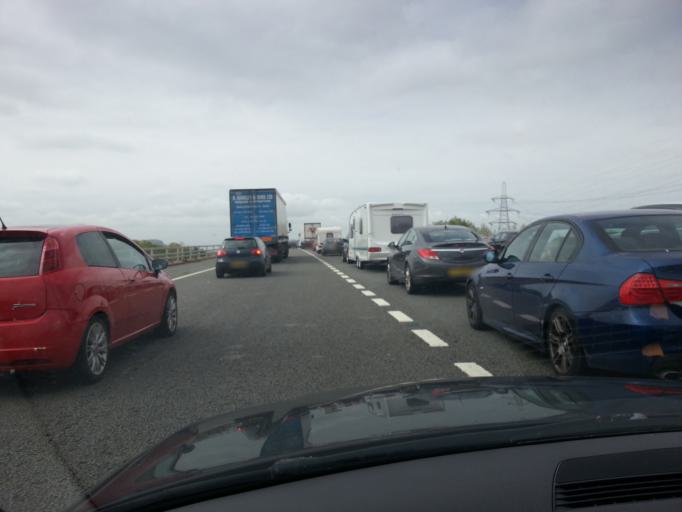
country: GB
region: England
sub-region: Borough of Halton
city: Halton
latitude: 53.3108
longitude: -2.7053
